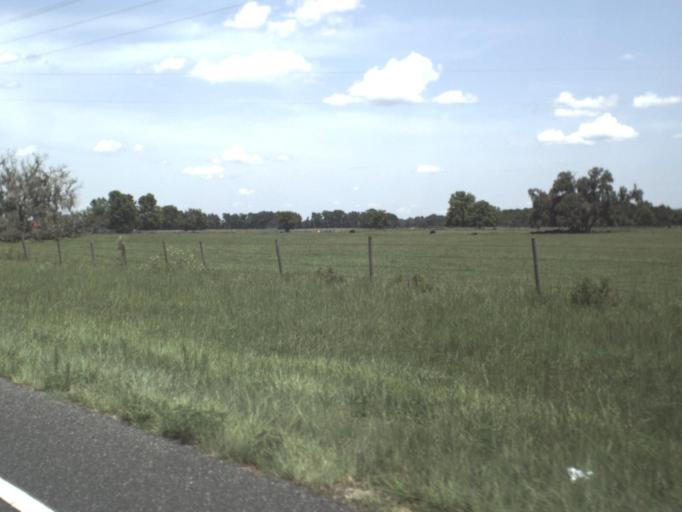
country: US
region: Florida
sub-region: Levy County
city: Chiefland
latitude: 29.4946
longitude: -82.8477
